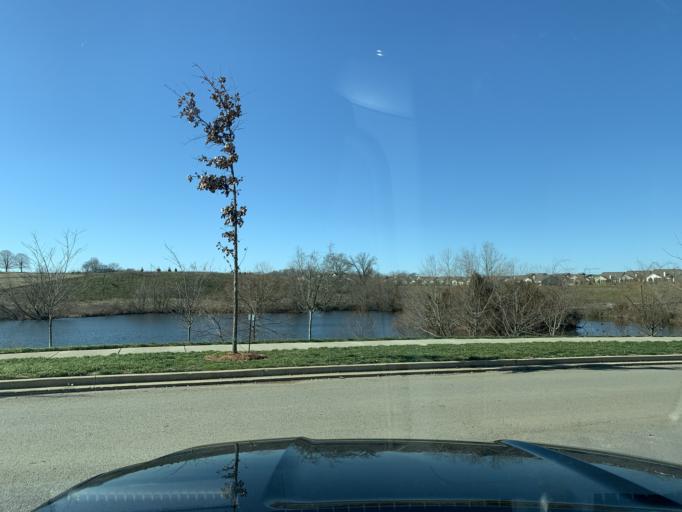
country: US
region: Tennessee
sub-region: Maury County
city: Spring Hill
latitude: 35.7258
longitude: -86.9270
